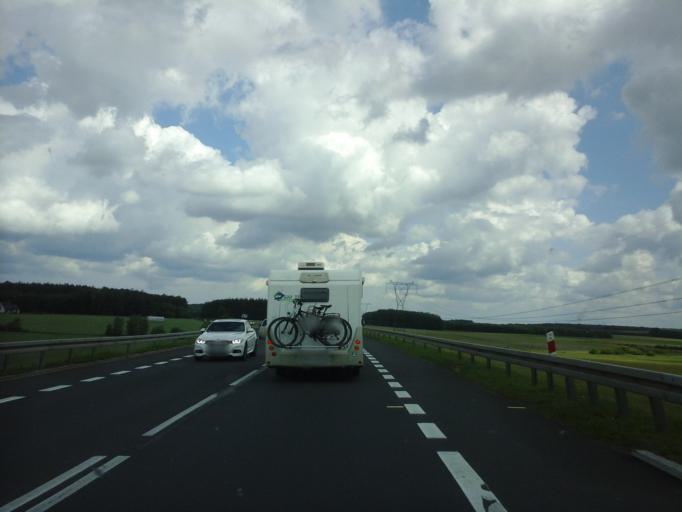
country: PL
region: West Pomeranian Voivodeship
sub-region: Powiat bialogardzki
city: Karlino
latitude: 54.0345
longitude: 15.8961
